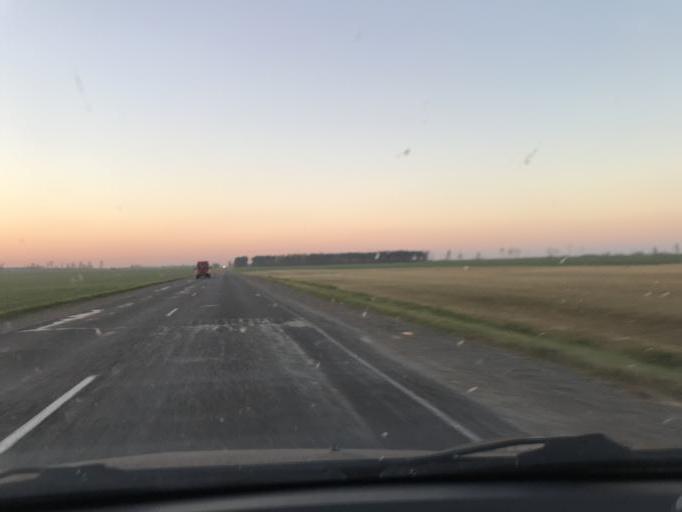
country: BY
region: Gomel
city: Horad Rechytsa
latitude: 52.1864
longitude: 30.5565
